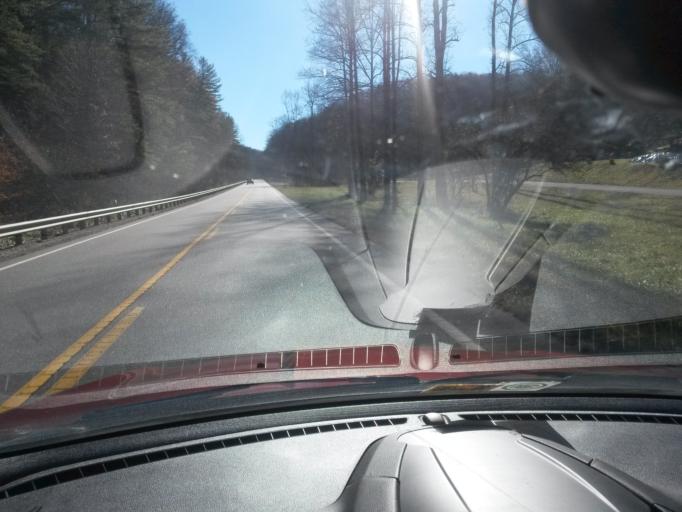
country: US
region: Virginia
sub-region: Henry County
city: Pannill Fork
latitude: 36.7798
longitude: -80.1223
